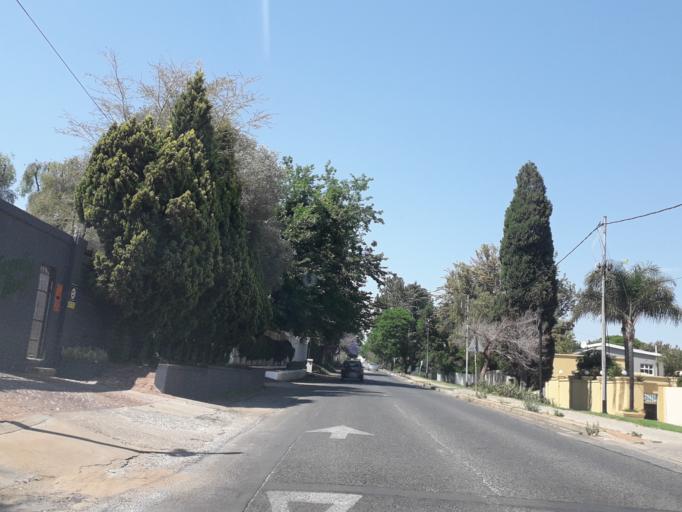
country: ZA
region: Gauteng
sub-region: City of Johannesburg Metropolitan Municipality
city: Johannesburg
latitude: -26.1192
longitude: 28.0211
